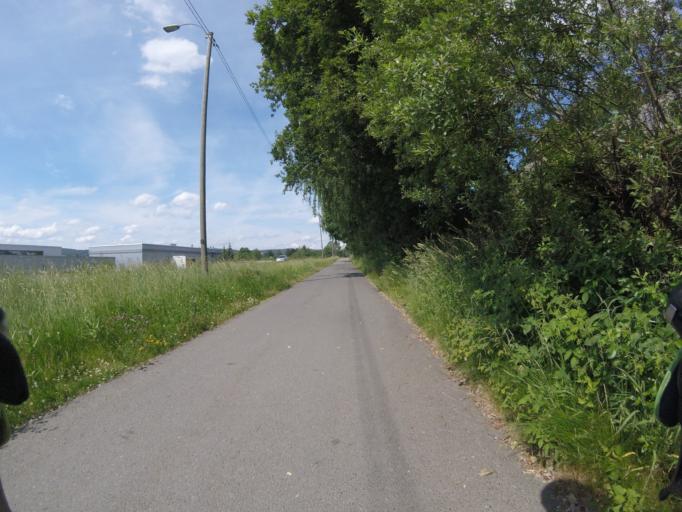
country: NO
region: Akershus
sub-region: Skedsmo
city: Lillestrom
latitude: 59.9749
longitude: 11.0312
